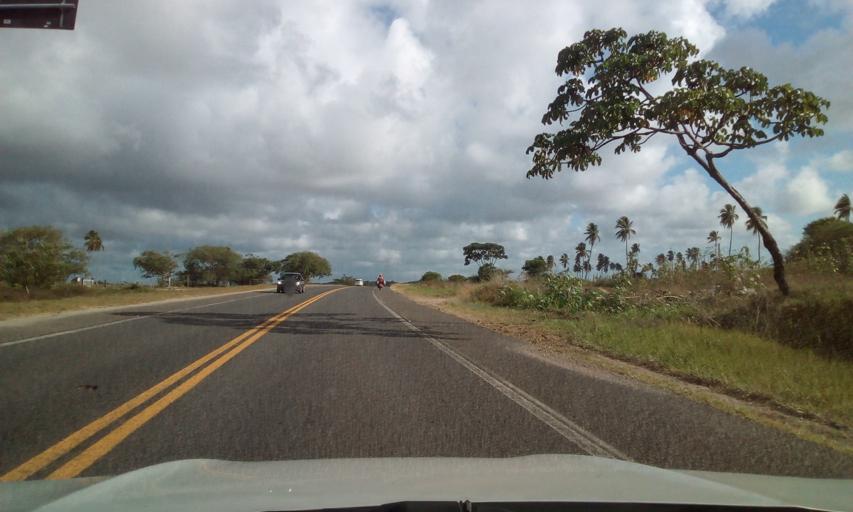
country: BR
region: Bahia
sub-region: Conde
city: Conde
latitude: -11.8168
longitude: -37.6353
